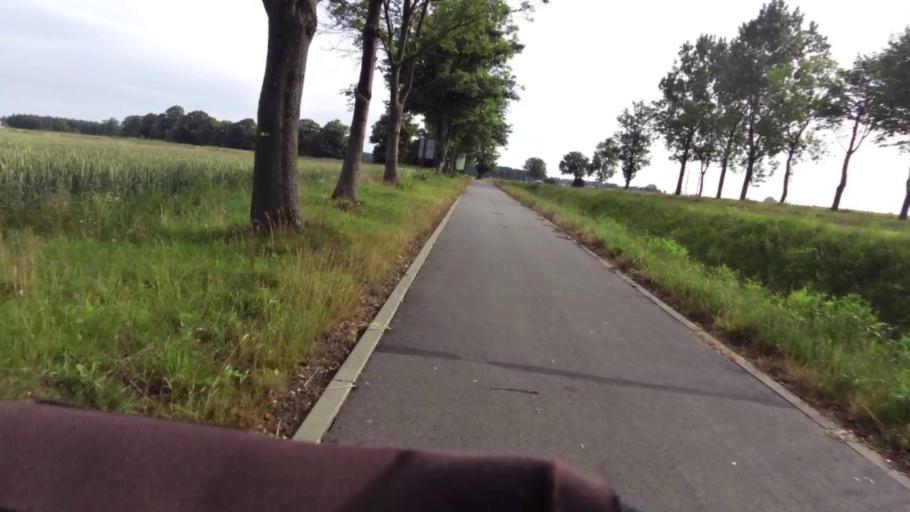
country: PL
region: West Pomeranian Voivodeship
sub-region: Powiat kamienski
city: Kamien Pomorski
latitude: 53.9848
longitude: 14.7985
